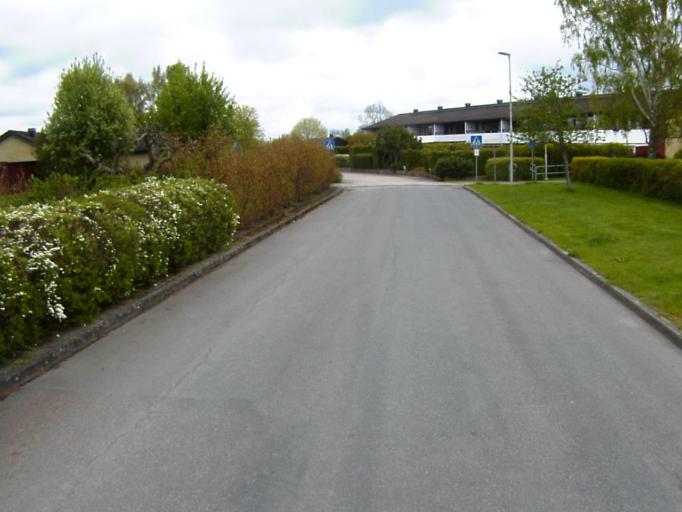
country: SE
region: Skane
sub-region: Kristianstads Kommun
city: Kristianstad
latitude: 56.0519
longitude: 14.1836
